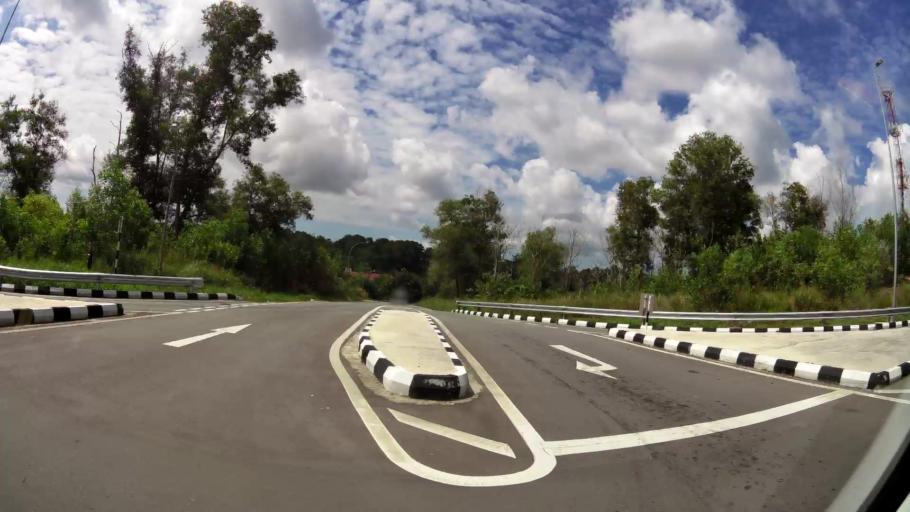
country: BN
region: Brunei and Muara
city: Bandar Seri Begawan
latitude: 4.9327
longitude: 114.8922
